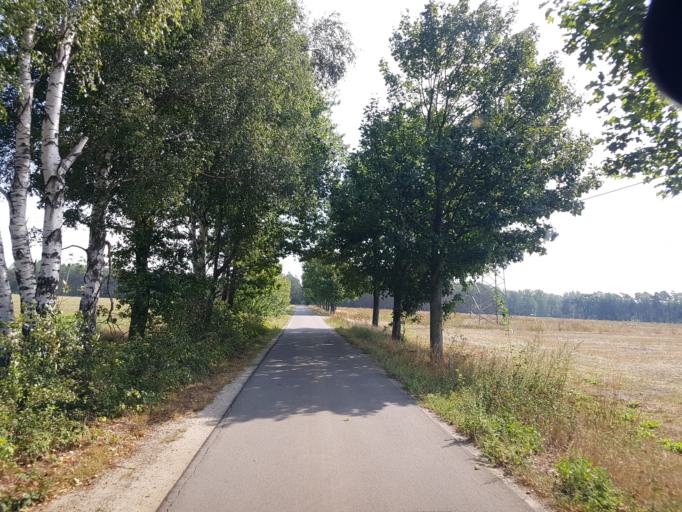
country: DE
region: Brandenburg
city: Finsterwalde
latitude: 51.6617
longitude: 13.7522
